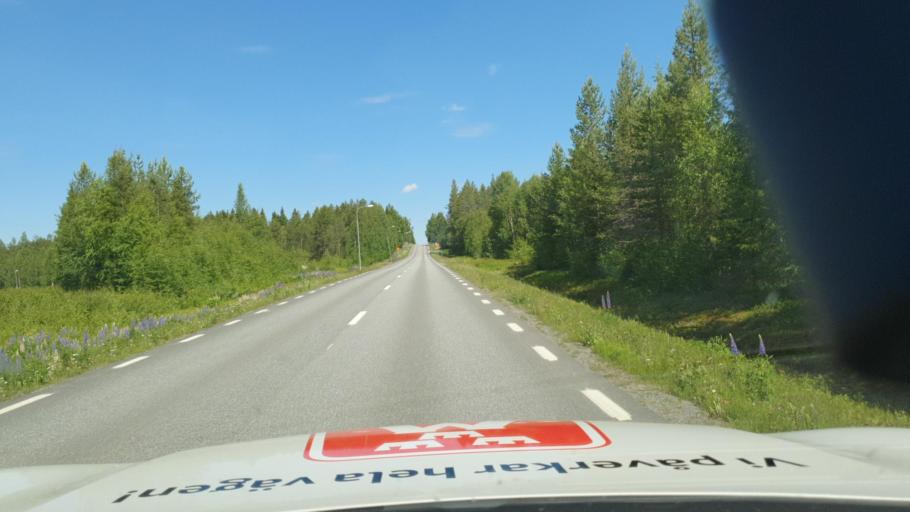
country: SE
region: Vaesterbotten
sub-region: Skelleftea Kommun
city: Boliden
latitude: 64.8549
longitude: 20.3814
